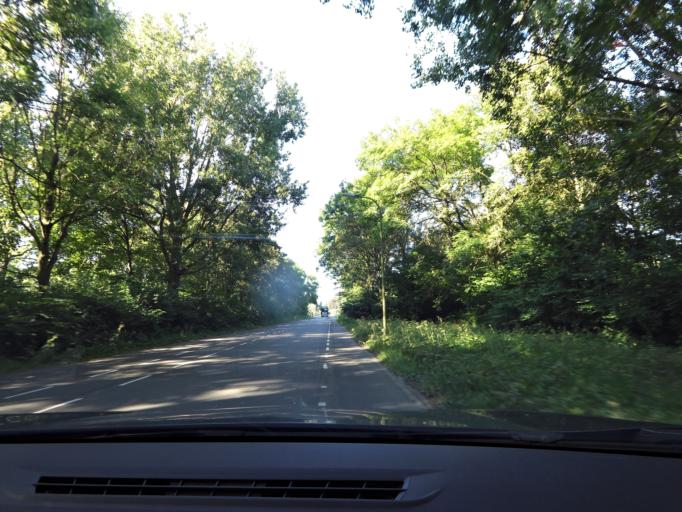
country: NL
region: South Holland
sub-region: Gemeente Dordrecht
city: Dordrecht
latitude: 51.7812
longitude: 4.6884
